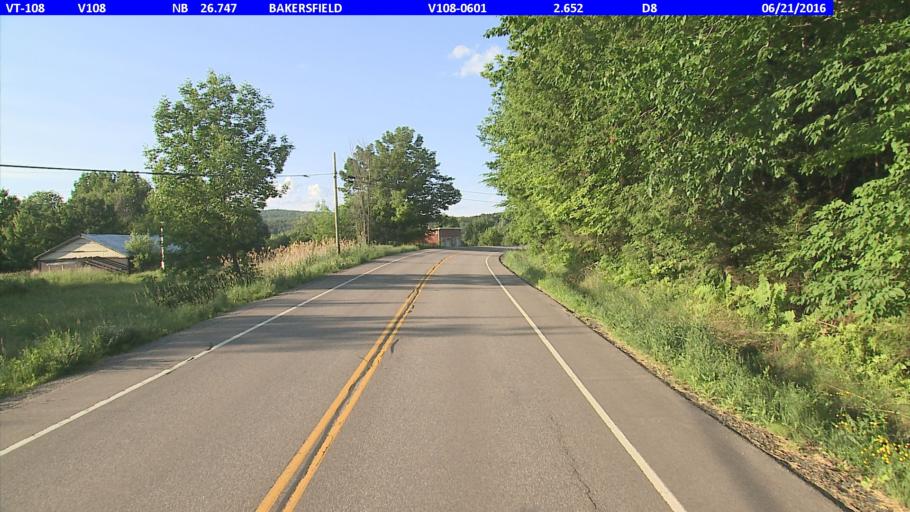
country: US
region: Vermont
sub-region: Franklin County
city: Enosburg Falls
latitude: 44.7696
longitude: -72.8119
